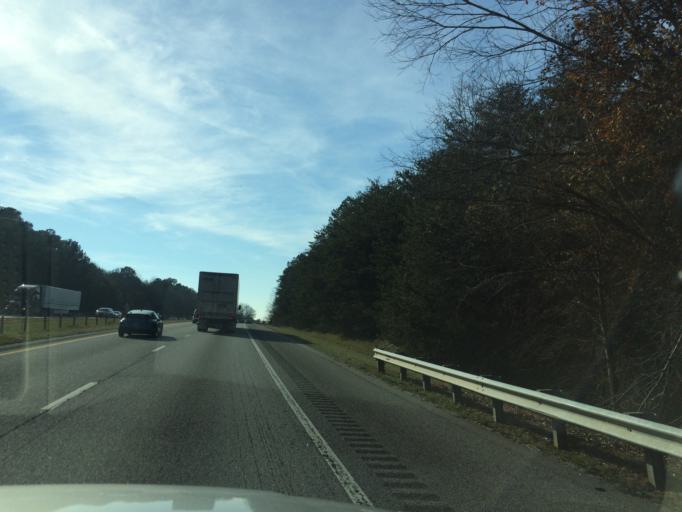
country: US
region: Georgia
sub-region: Hart County
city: Reed Creek
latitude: 34.5310
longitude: -82.8346
